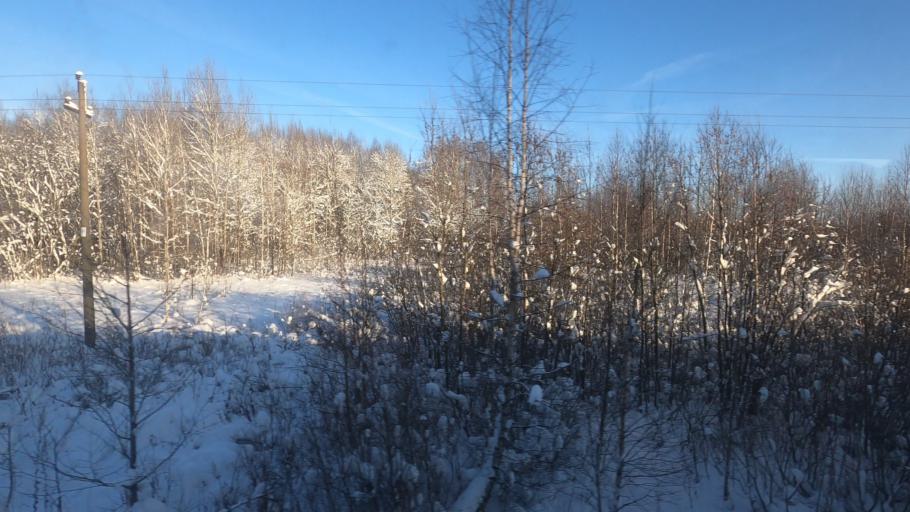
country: RU
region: Moskovskaya
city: Taldom
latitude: 56.7105
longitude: 37.5413
